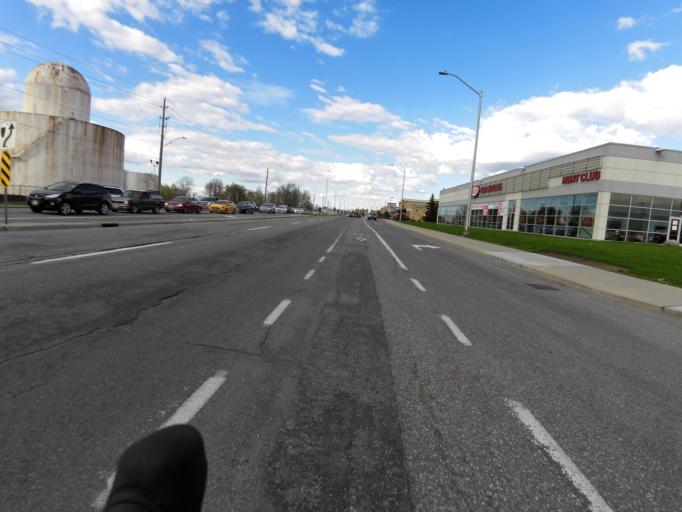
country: CA
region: Ontario
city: Ottawa
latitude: 45.3377
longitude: -75.7171
